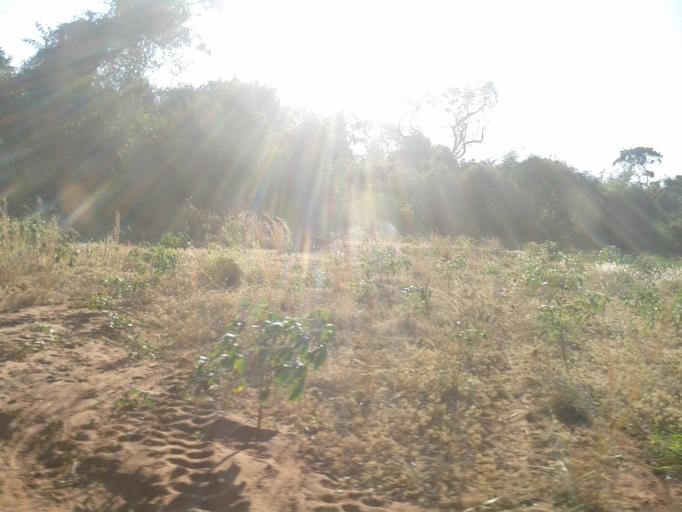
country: BR
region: Minas Gerais
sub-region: Centralina
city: Centralina
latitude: -18.7491
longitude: -49.0948
